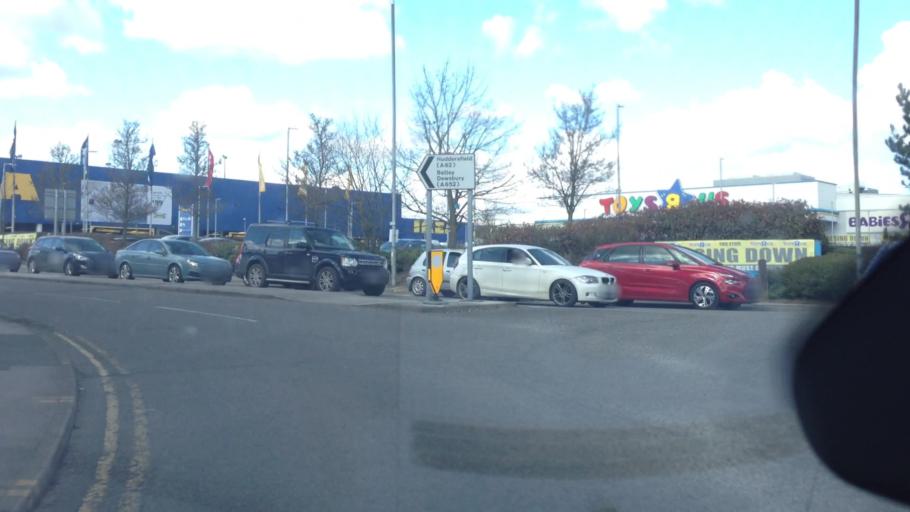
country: GB
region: England
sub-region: City and Borough of Leeds
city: Gildersome
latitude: 53.7448
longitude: -1.6455
